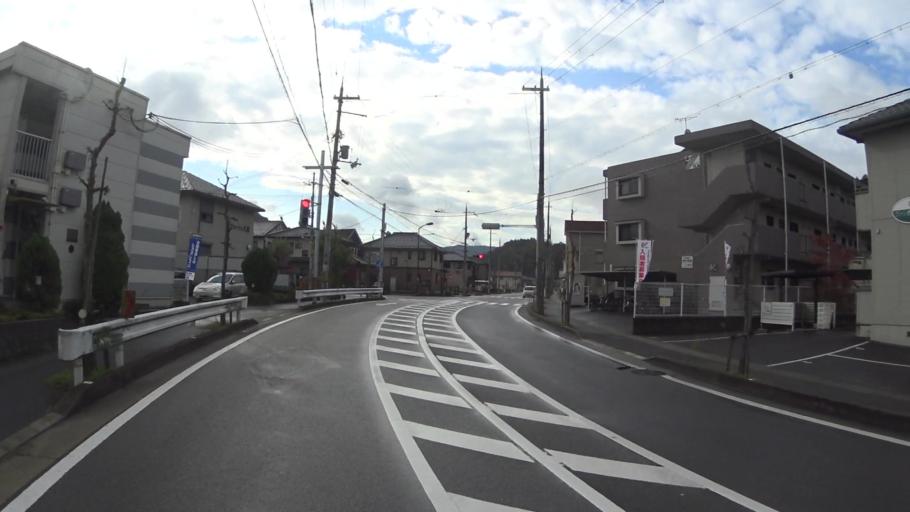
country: JP
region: Kyoto
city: Ayabe
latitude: 35.3002
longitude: 135.2343
